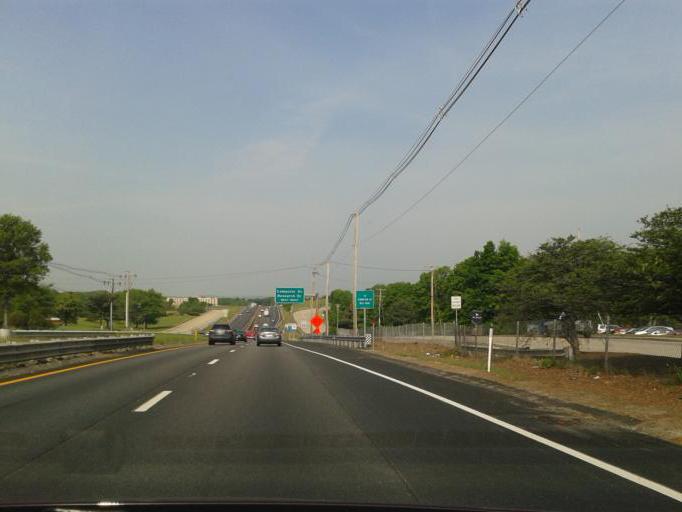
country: US
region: Massachusetts
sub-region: Worcester County
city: Westborough
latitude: 42.2887
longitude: -71.5735
